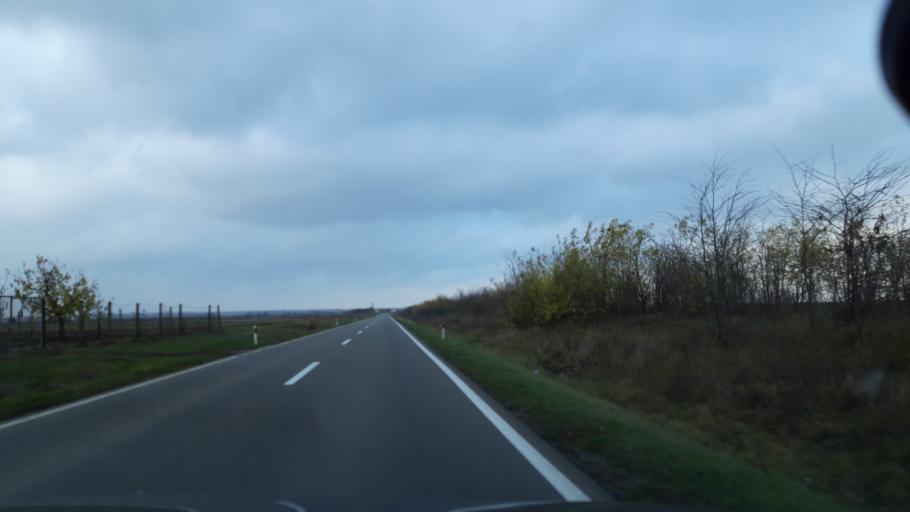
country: RS
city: Sanad
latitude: 45.9943
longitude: 20.1060
